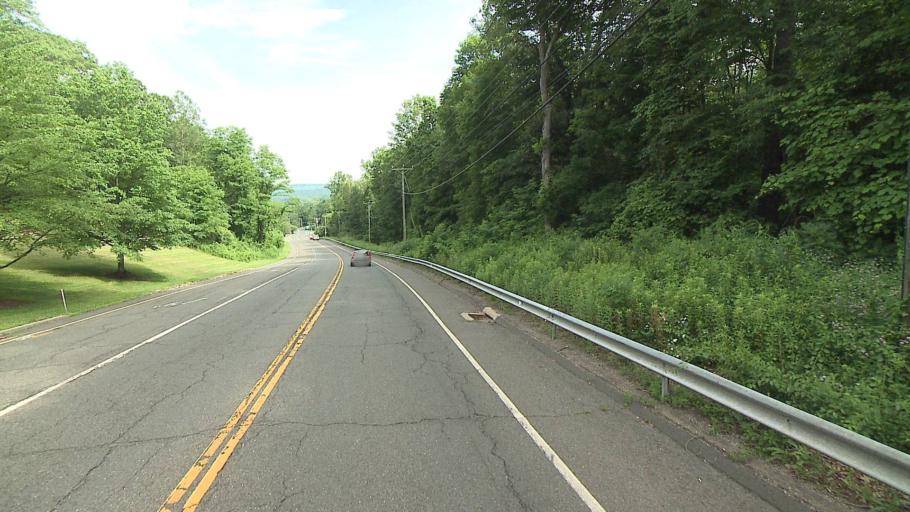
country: US
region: Connecticut
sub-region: New Haven County
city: Southbury
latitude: 41.4728
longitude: -73.2072
